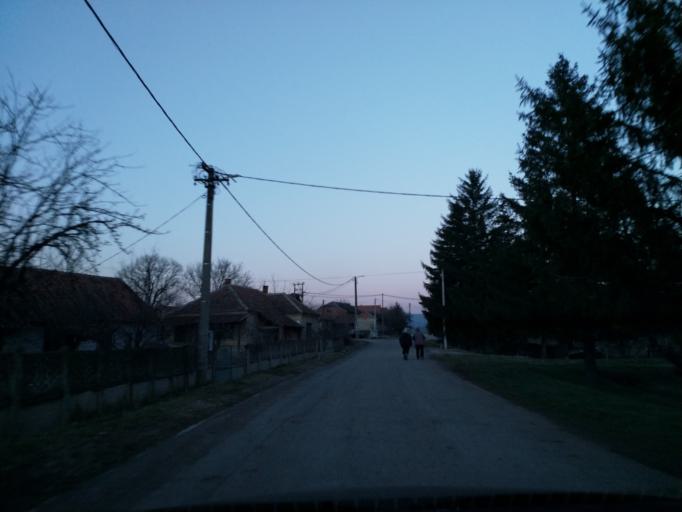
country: RS
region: Central Serbia
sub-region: Pomoravski Okrug
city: Paracin
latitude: 43.8659
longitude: 21.4764
